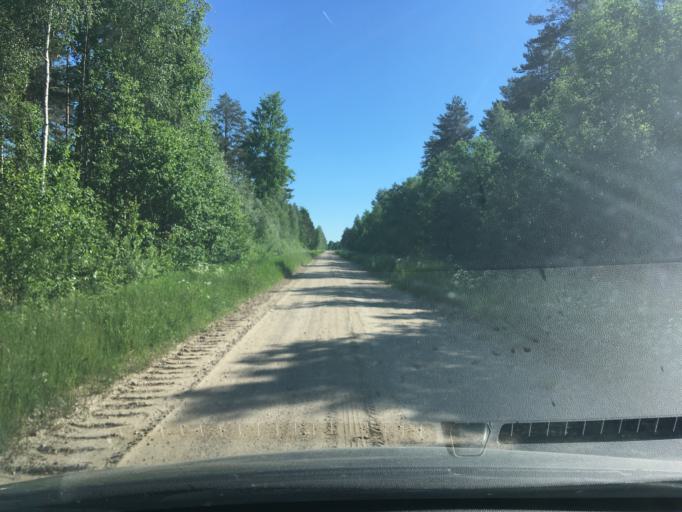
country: EE
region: Laeaene
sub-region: Lihula vald
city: Lihula
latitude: 58.6405
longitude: 23.7661
